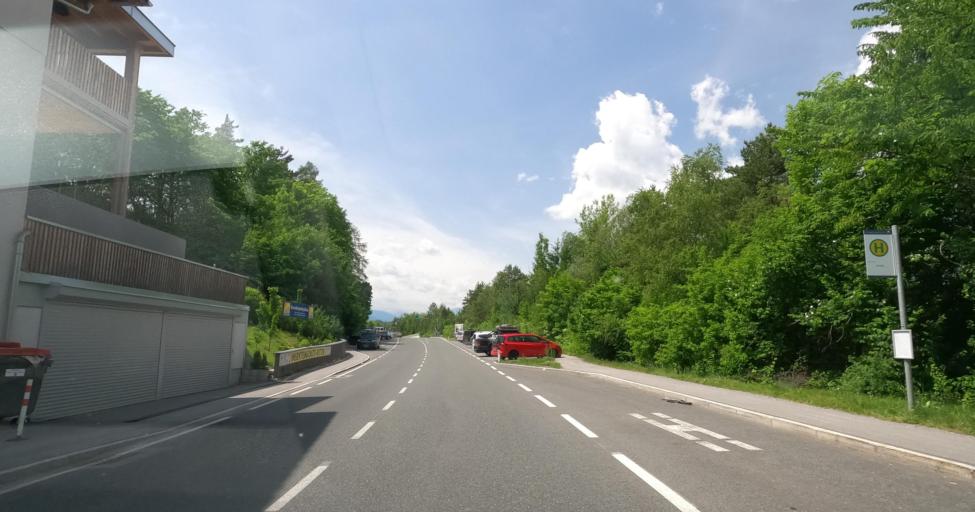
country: AT
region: Tyrol
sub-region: Politischer Bezirk Innsbruck Land
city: Hall in Tirol
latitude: 47.2763
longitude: 11.5084
